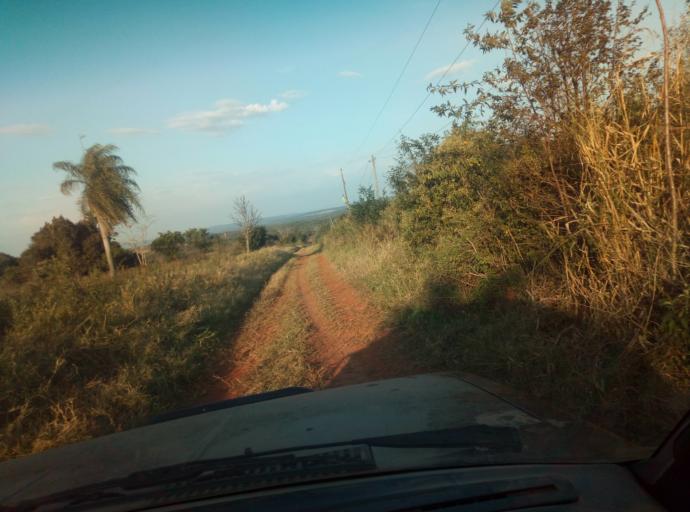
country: PY
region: Caaguazu
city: Doctor Cecilio Baez
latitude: -25.1527
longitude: -56.2426
